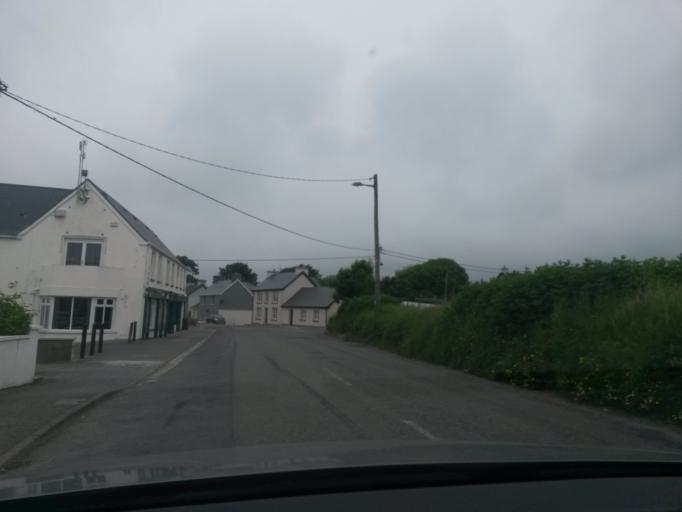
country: IE
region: Munster
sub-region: Ciarrai
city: Ballybunnion
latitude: 52.4508
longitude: -9.6636
